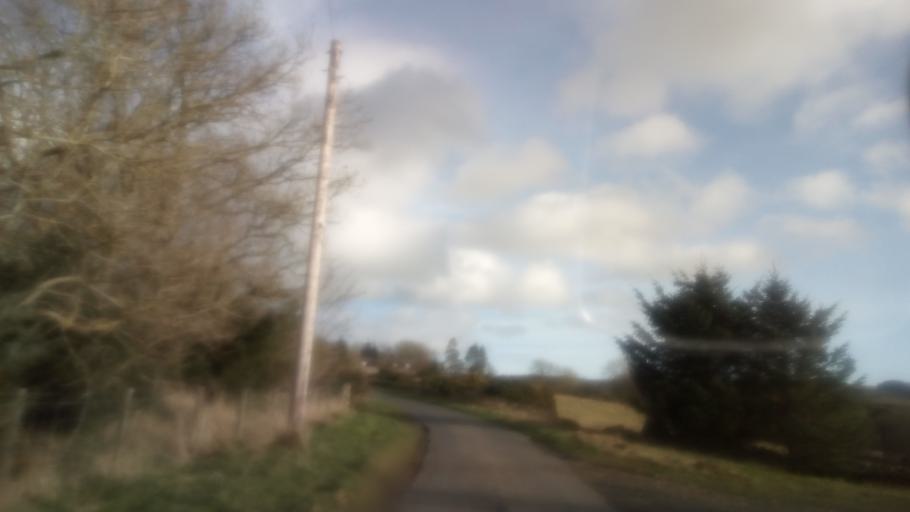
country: GB
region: Scotland
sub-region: The Scottish Borders
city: Jedburgh
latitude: 55.4734
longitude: -2.6146
